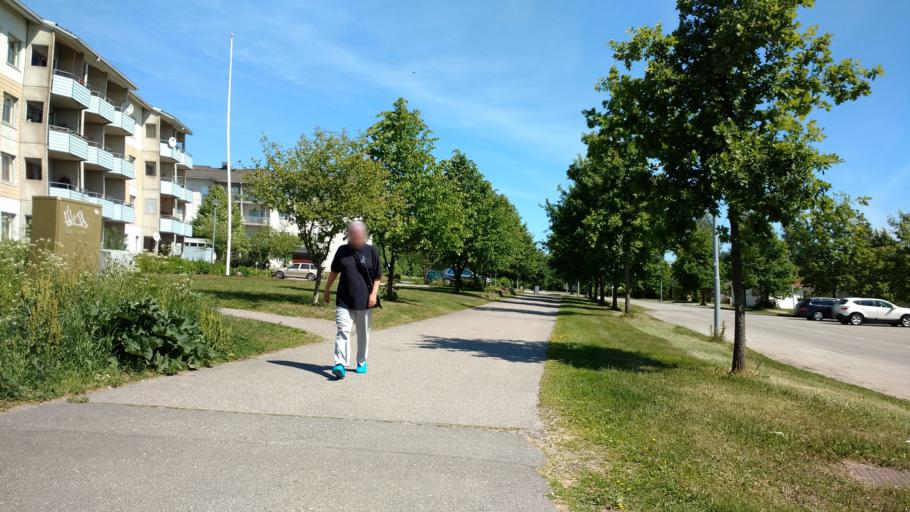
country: FI
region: Varsinais-Suomi
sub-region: Salo
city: Salo
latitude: 60.4017
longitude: 23.1405
